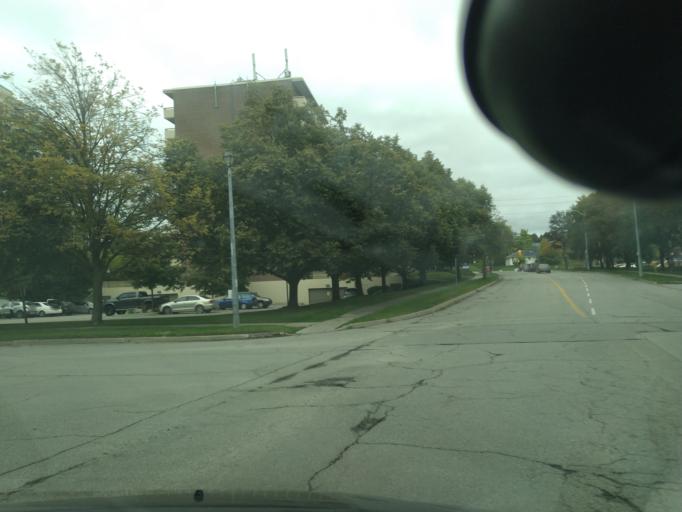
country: CA
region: Ontario
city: Newmarket
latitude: 44.0567
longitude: -79.4659
